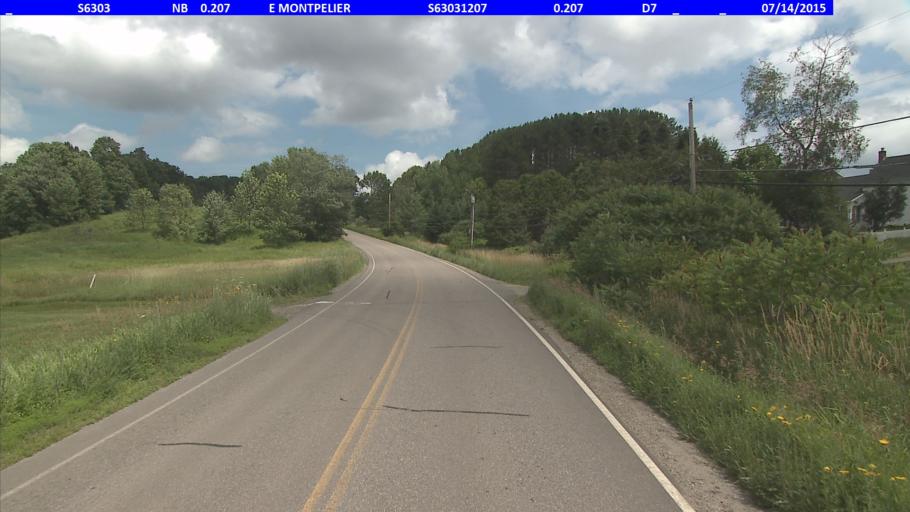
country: US
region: Vermont
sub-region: Washington County
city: Montpelier
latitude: 44.2746
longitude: -72.5539
